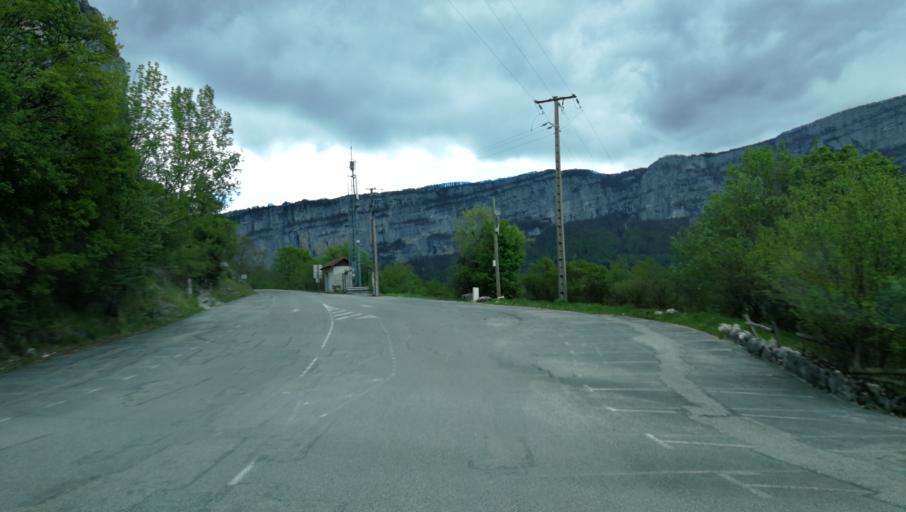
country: FR
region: Rhone-Alpes
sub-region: Departement de l'Isere
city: Pont-en-Royans
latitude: 45.0707
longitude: 5.3976
